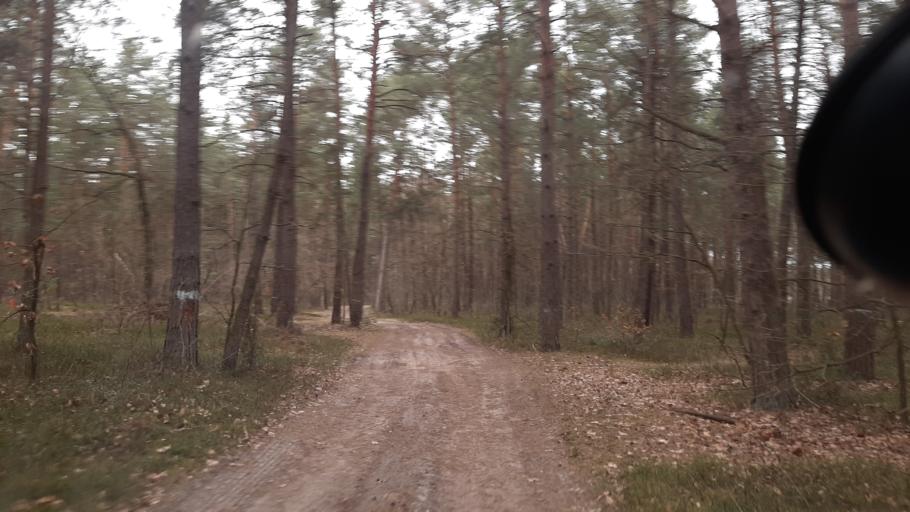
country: PL
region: Lublin Voivodeship
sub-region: Powiat lubartowski
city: Abramow
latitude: 51.4318
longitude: 22.3441
